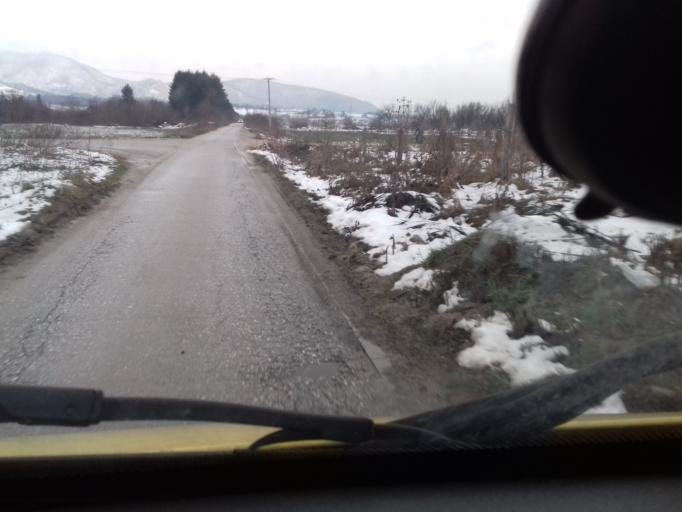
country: BA
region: Federation of Bosnia and Herzegovina
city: Vitez
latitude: 44.1577
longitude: 17.7793
